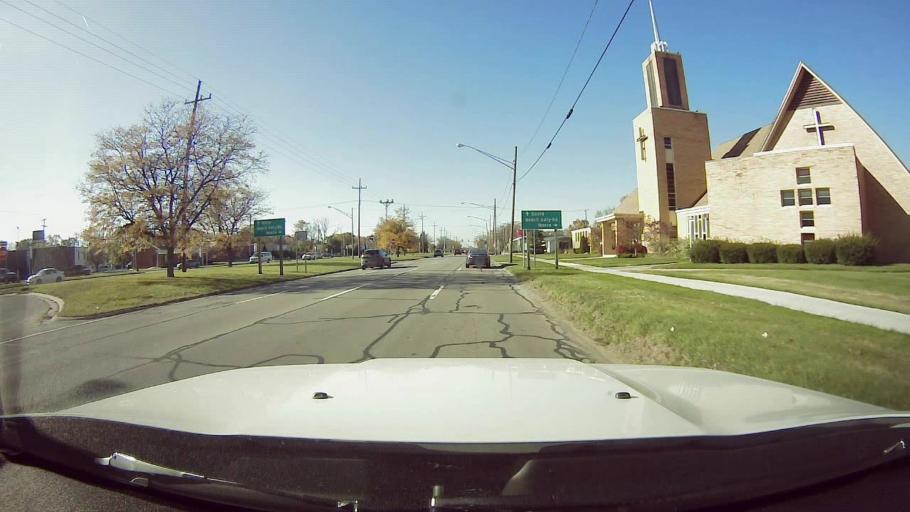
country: US
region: Michigan
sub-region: Wayne County
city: Redford
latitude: 42.4317
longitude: -83.2949
